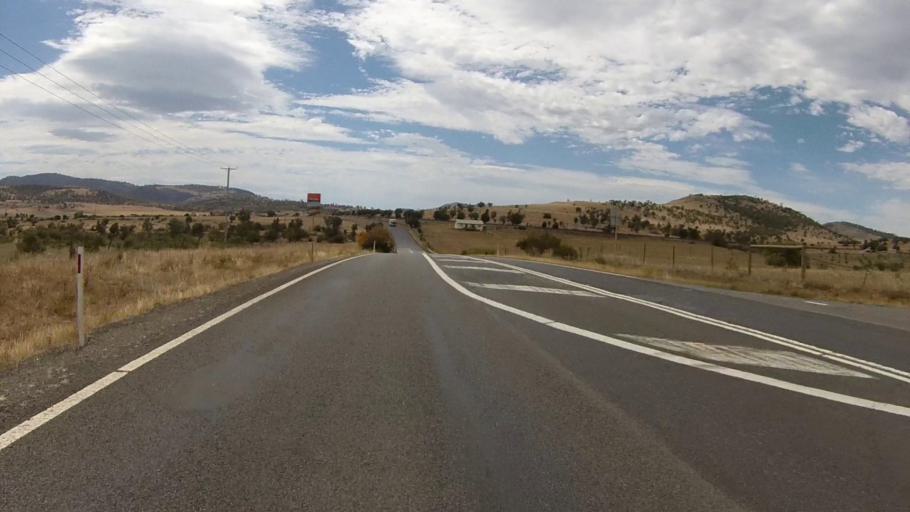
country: AU
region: Tasmania
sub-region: Brighton
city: Bridgewater
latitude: -42.6924
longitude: 147.2939
